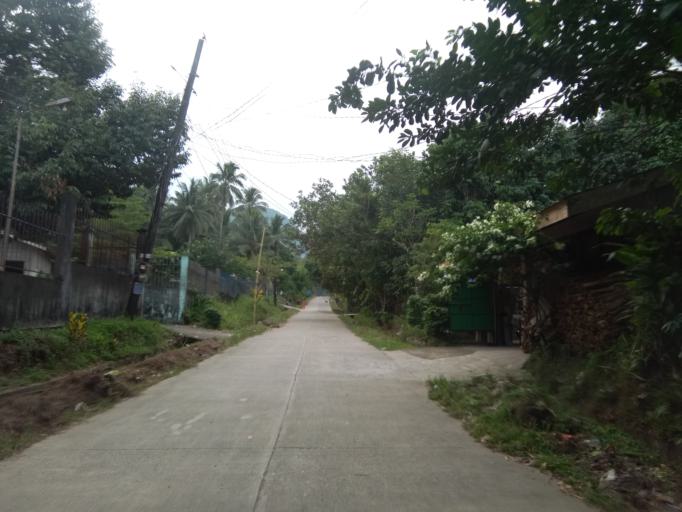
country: PH
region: Caraga
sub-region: Province of Surigao del Norte
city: Tubod
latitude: 9.5654
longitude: 125.5688
